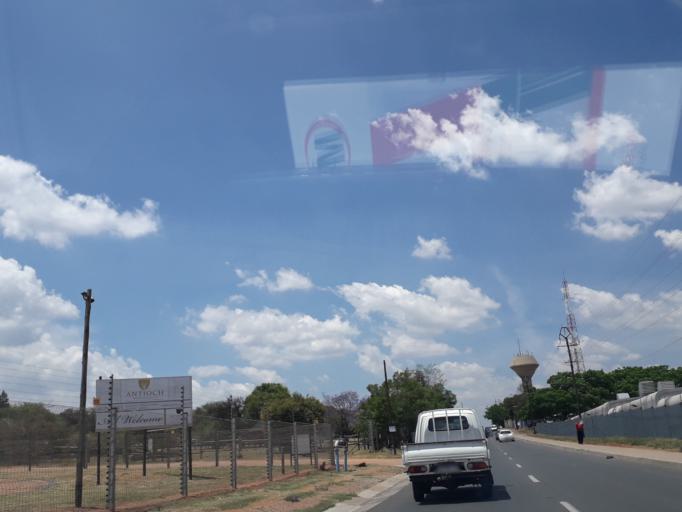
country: ZA
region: Gauteng
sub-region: West Rand District Municipality
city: Muldersdriseloop
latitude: -26.0742
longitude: 27.9251
